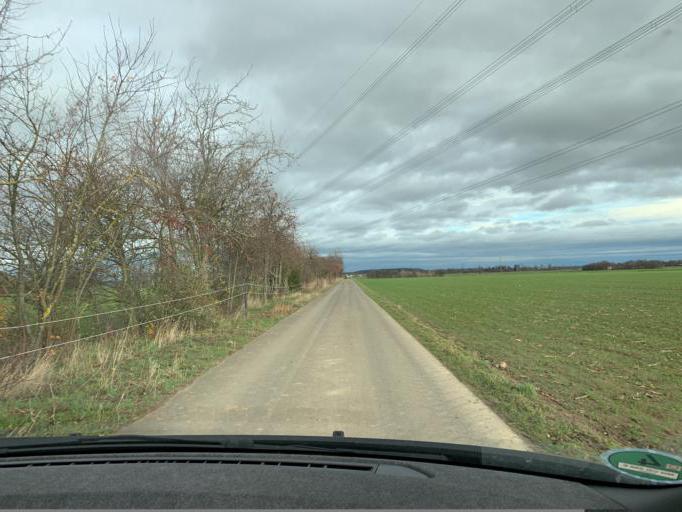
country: DE
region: North Rhine-Westphalia
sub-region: Regierungsbezirk Koln
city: Dueren
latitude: 50.7803
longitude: 6.5258
